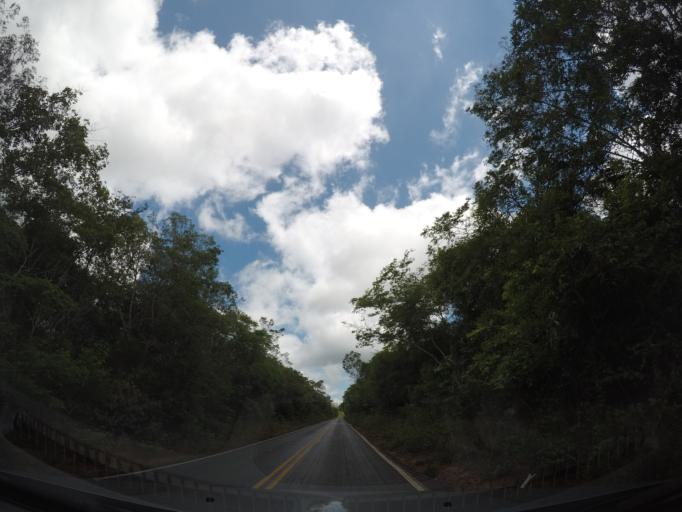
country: BR
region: Bahia
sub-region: Andarai
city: Vera Cruz
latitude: -12.5255
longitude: -41.3633
